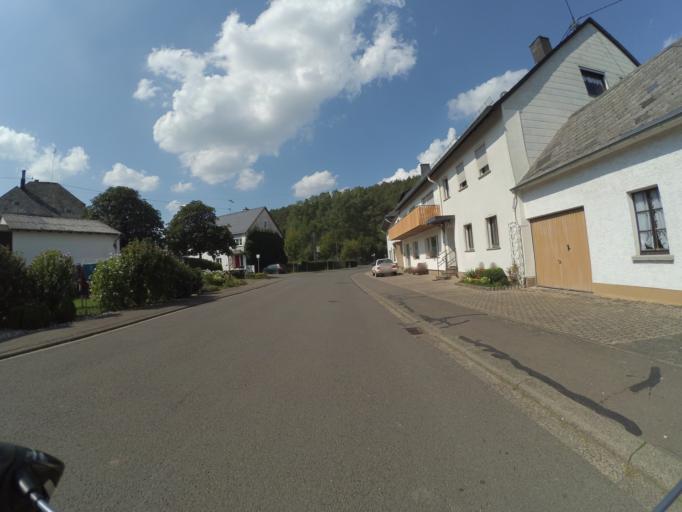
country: DE
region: Rheinland-Pfalz
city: Morbach
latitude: 49.8214
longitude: 7.1474
